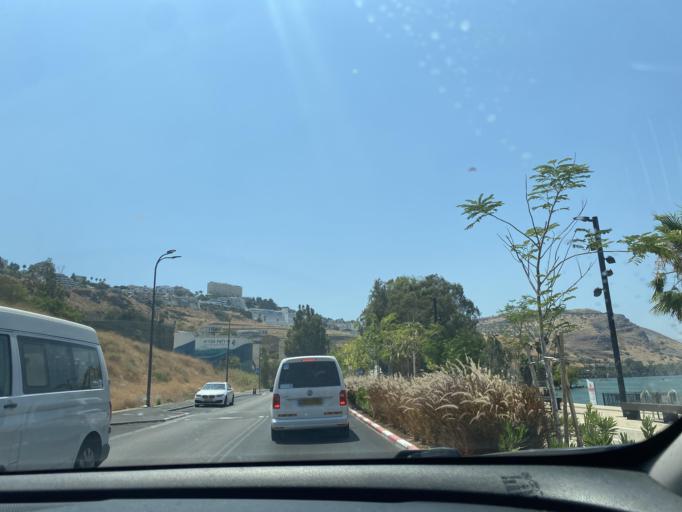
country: IL
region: Northern District
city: Tiberias
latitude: 32.8012
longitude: 35.5355
